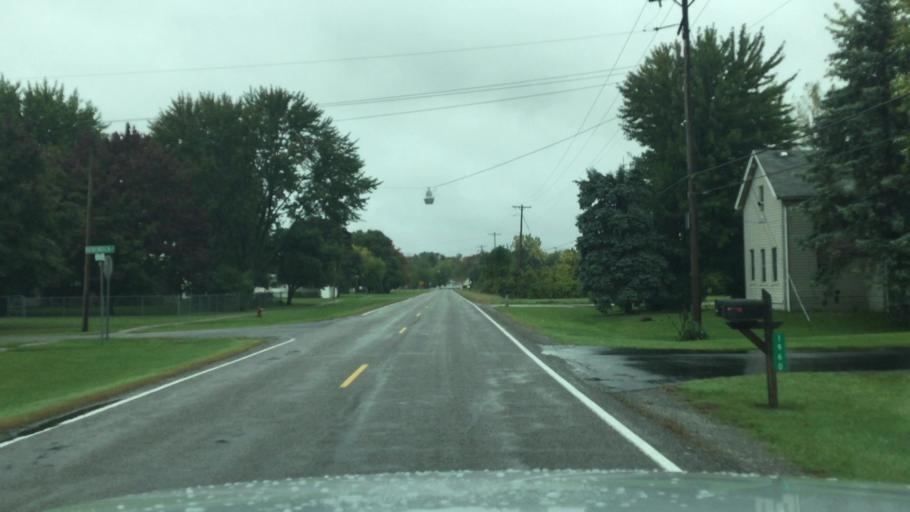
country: US
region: Michigan
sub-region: Saginaw County
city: Carrollton
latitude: 43.4693
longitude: -83.9408
